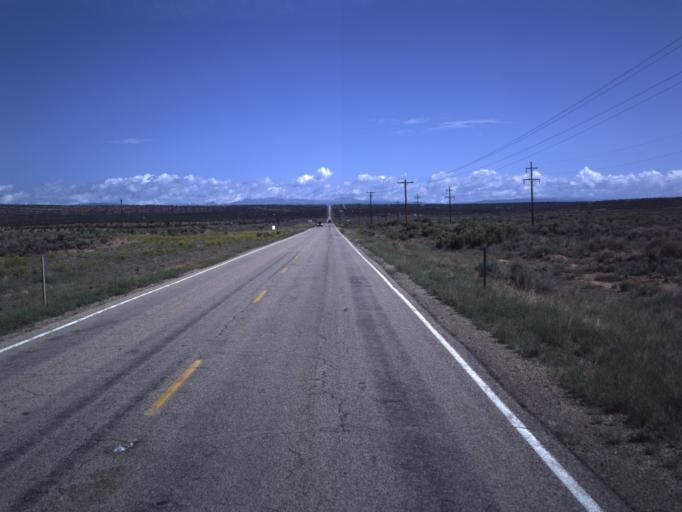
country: US
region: Utah
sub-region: Duchesne County
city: Duchesne
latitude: 40.2617
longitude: -110.3833
